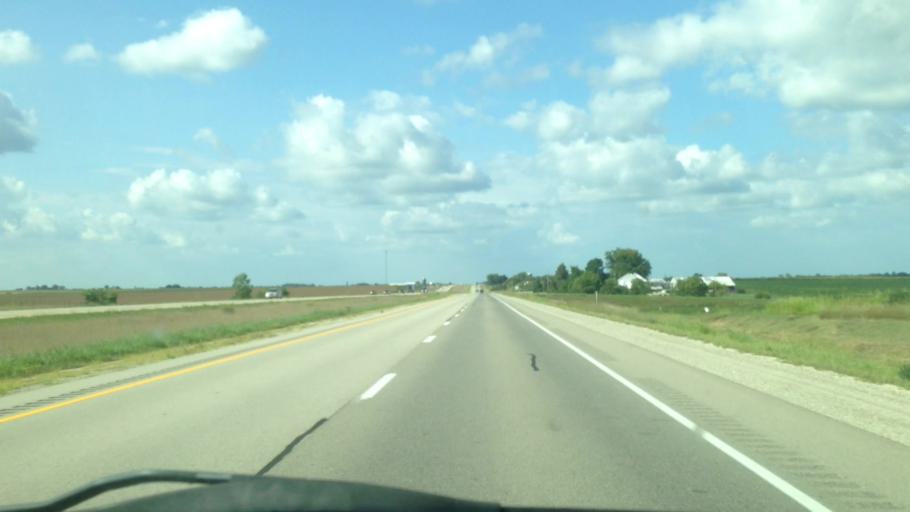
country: US
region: Iowa
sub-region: Henry County
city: Mount Pleasant
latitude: 40.7961
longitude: -91.5643
